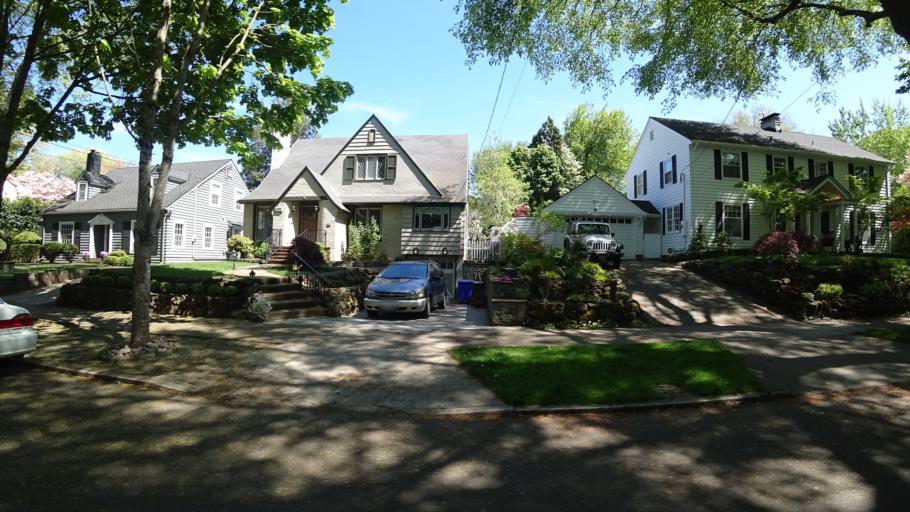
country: US
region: Oregon
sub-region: Clackamas County
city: Milwaukie
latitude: 45.4755
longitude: -122.6283
